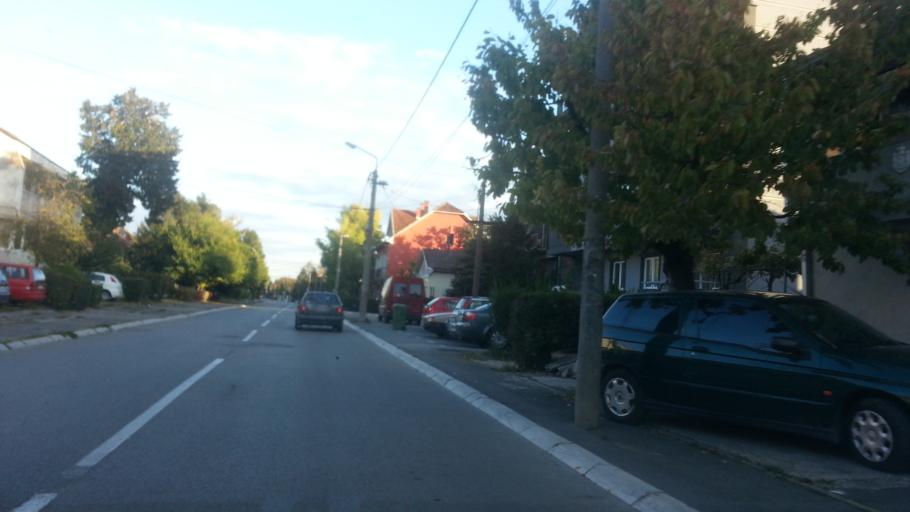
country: RS
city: Novi Banovci
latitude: 44.8990
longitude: 20.2810
